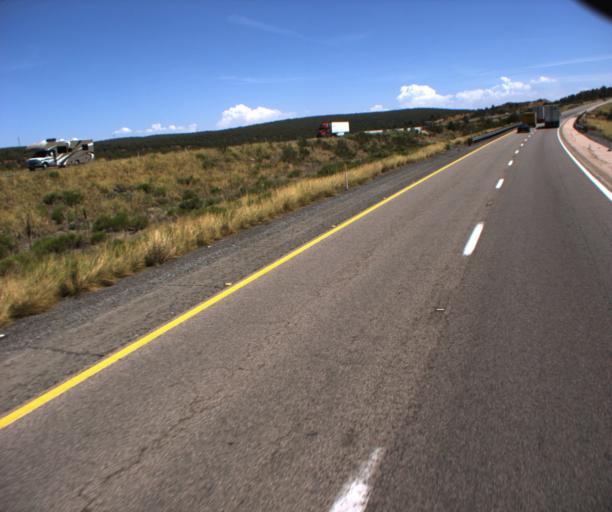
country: US
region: Arizona
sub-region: Mohave County
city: Peach Springs
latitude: 35.2039
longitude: -113.2993
